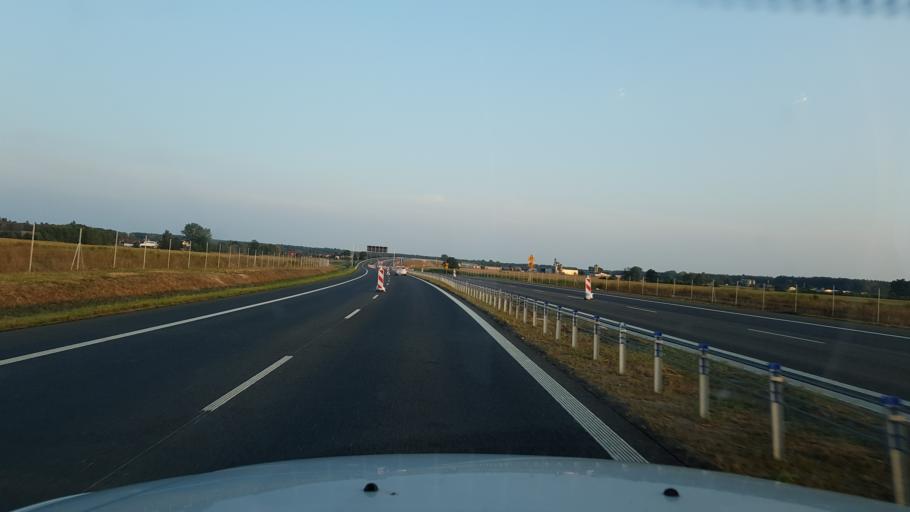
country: PL
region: West Pomeranian Voivodeship
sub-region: Powiat gryficki
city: Ploty
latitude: 53.8061
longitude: 15.2484
